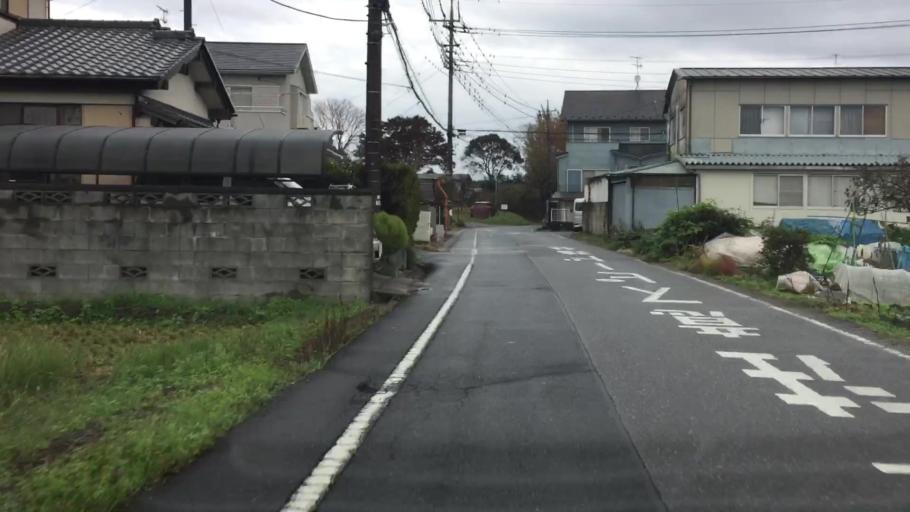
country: JP
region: Ibaraki
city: Toride
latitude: 35.8682
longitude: 140.1180
